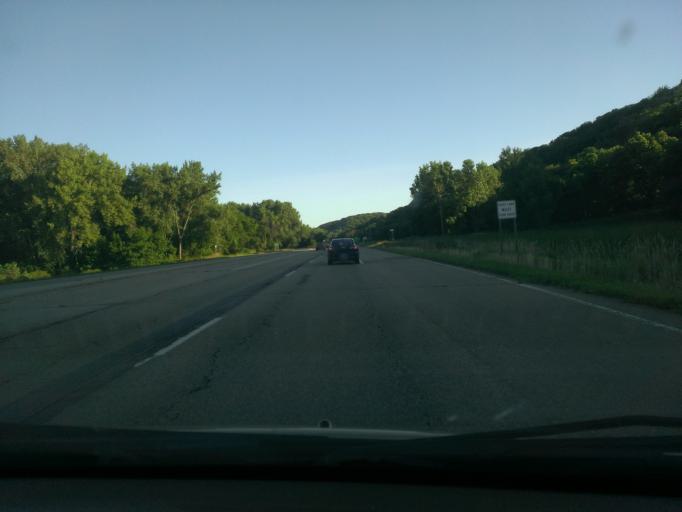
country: US
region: Minnesota
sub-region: Nicollet County
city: North Mankato
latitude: 44.2261
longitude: -94.0275
